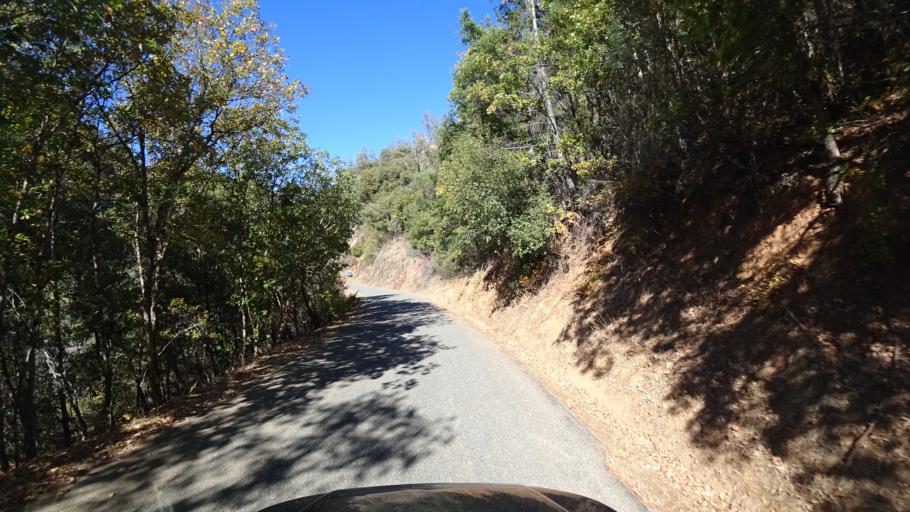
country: US
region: California
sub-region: Humboldt County
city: Willow Creek
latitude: 41.2190
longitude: -123.2381
